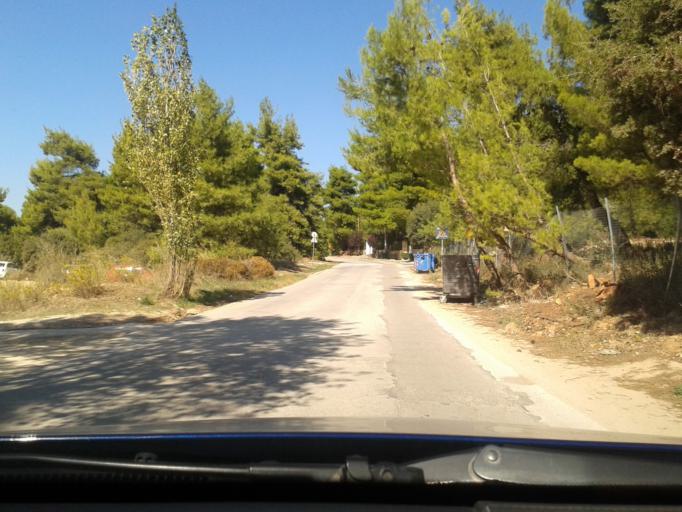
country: GR
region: Attica
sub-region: Nomarchia Anatolikis Attikis
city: Drosia
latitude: 38.1103
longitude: 23.8719
